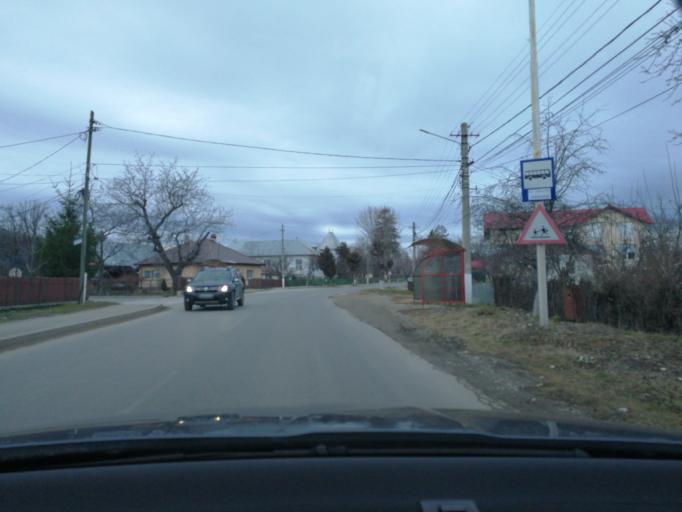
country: RO
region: Prahova
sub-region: Oras Breaza
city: Breaza de Jos
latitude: 45.1703
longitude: 25.6758
